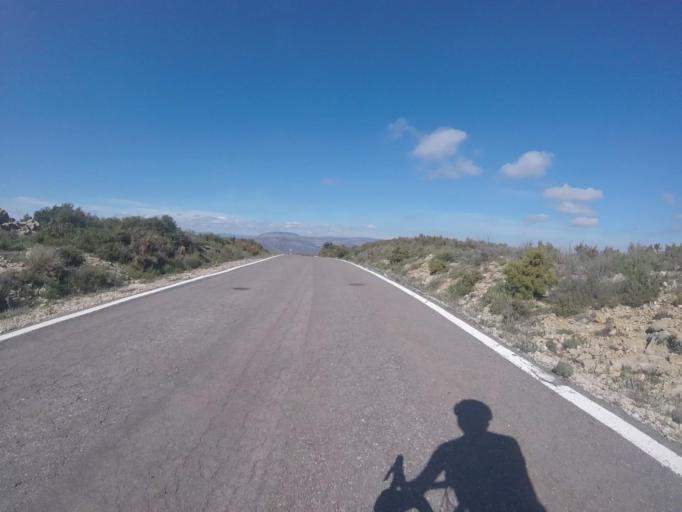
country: ES
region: Valencia
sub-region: Provincia de Castello
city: Albocasser
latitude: 40.3456
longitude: 0.0487
